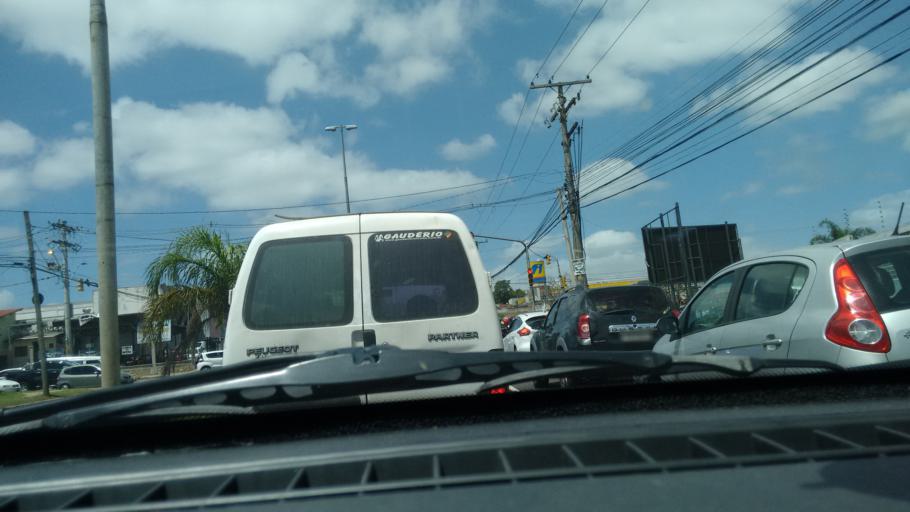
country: BR
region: Rio Grande do Sul
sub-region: Cachoeirinha
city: Cachoeirinha
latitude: -30.0193
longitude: -51.1197
